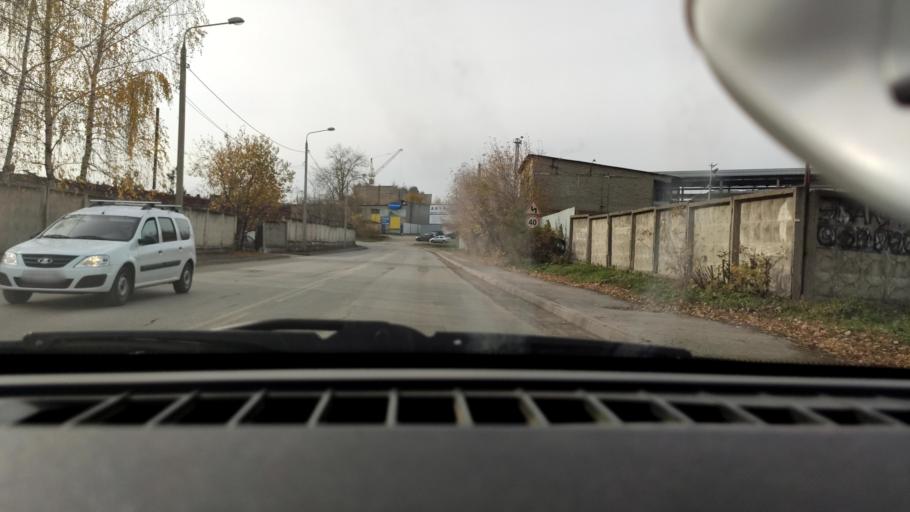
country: RU
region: Perm
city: Perm
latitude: 57.9829
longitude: 56.2730
